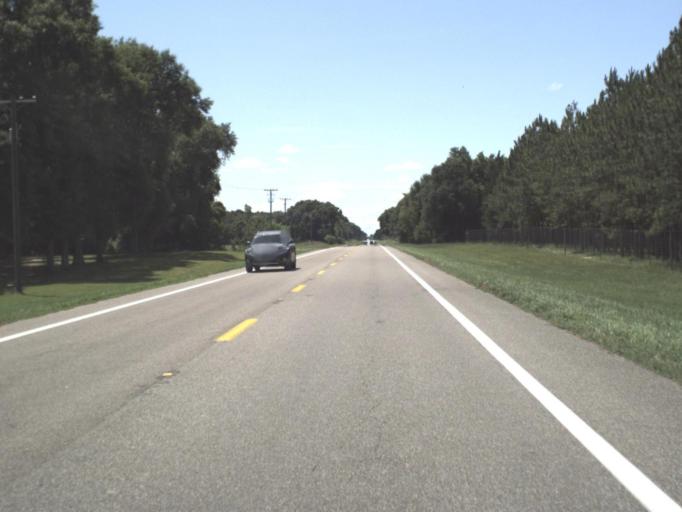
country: US
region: Florida
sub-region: Lafayette County
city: Mayo
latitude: 30.0250
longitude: -83.0525
